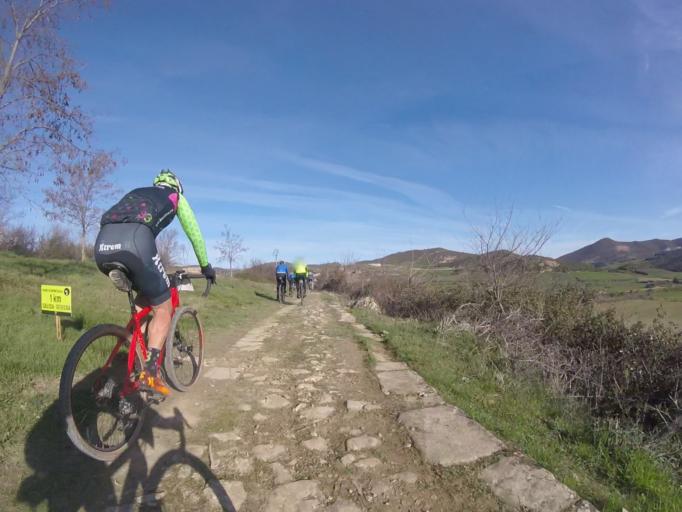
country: ES
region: Navarre
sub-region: Provincia de Navarra
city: Yerri
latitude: 42.6883
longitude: -1.9571
